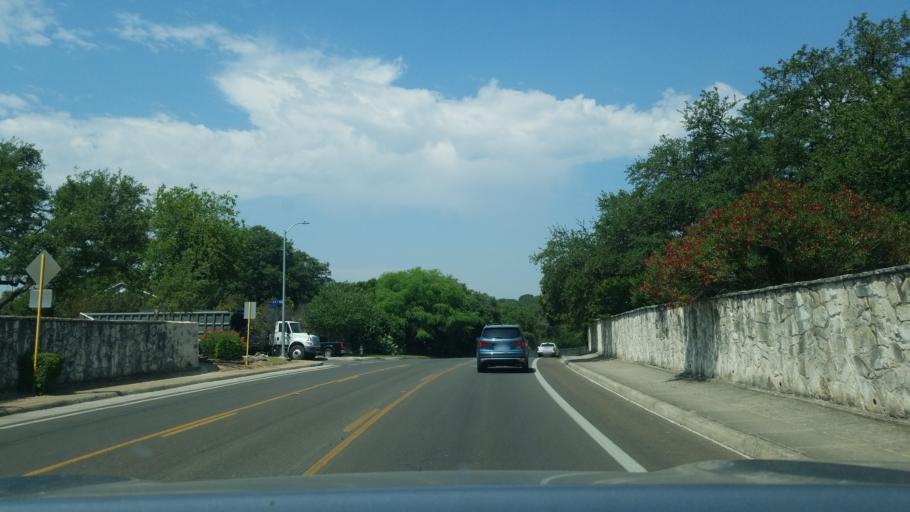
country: US
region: Texas
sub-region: Bexar County
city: Hollywood Park
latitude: 29.6300
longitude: -98.4466
